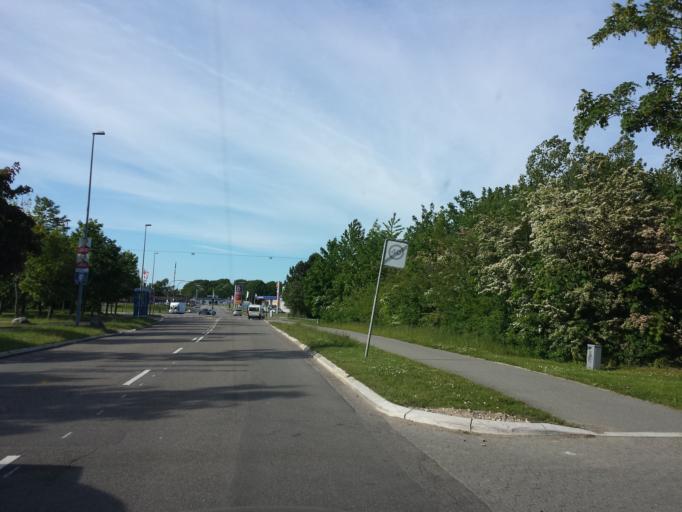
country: DK
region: Capital Region
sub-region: Ballerup Kommune
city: Ballerup
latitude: 55.7210
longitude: 12.3763
